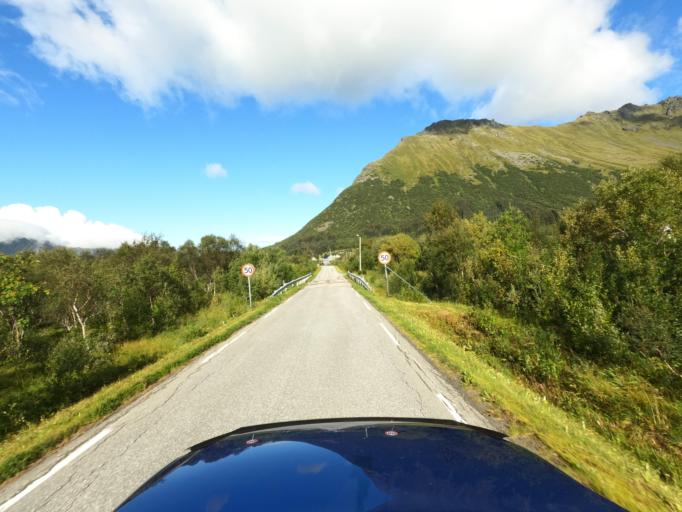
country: NO
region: Nordland
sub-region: Vagan
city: Kabelvag
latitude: 68.2832
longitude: 14.3493
